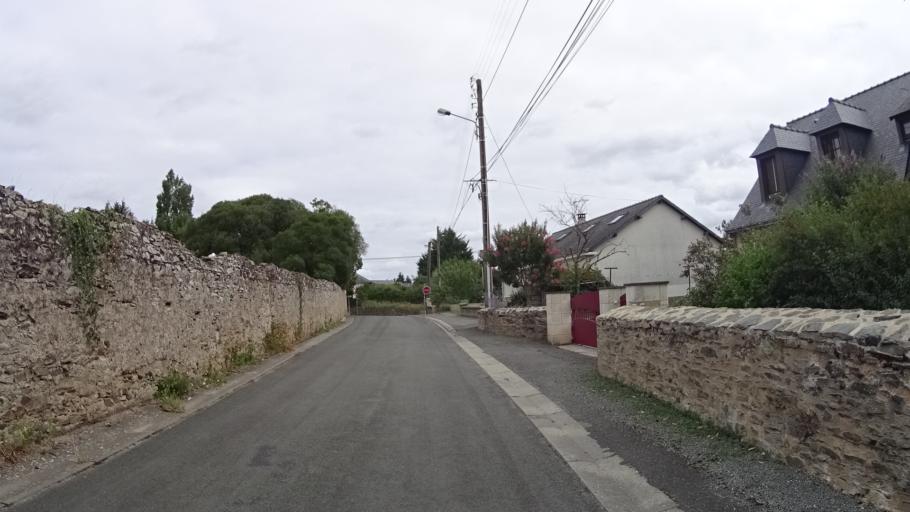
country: FR
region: Pays de la Loire
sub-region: Departement de Maine-et-Loire
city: Savennieres
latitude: 47.3837
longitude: -0.6660
